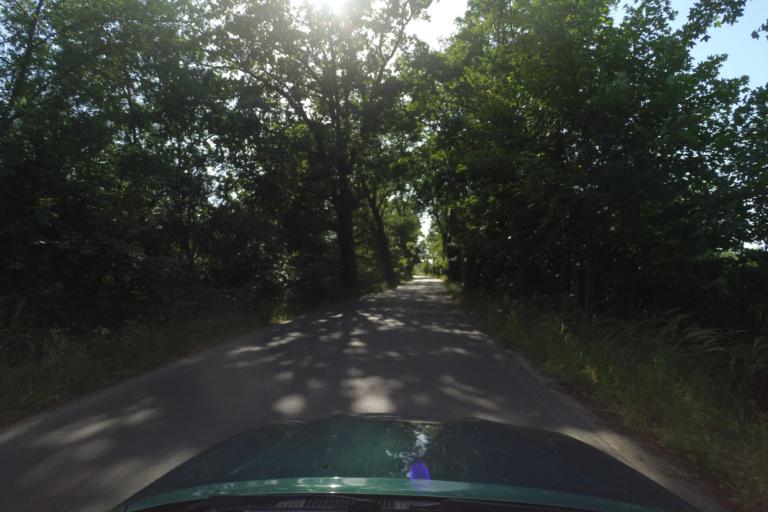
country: PL
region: Lower Silesian Voivodeship
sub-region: Powiat lubanski
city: Luban
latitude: 51.1203
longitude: 15.3195
